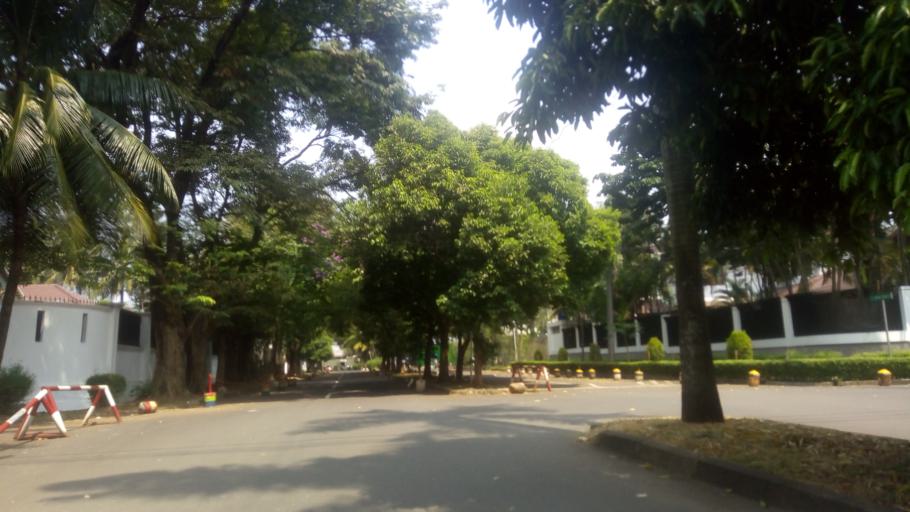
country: ID
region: Jakarta Raya
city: Jakarta
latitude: -6.2360
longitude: 106.8331
